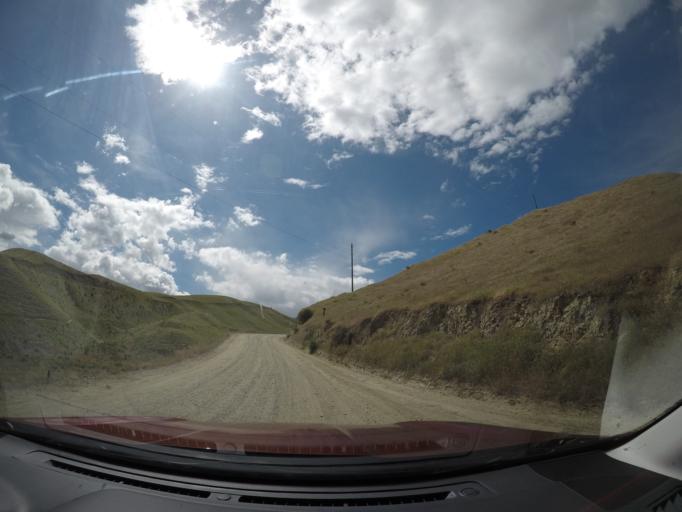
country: US
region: Washington
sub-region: Chelan County
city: West Wenatchee
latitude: 47.4607
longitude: -120.3532
